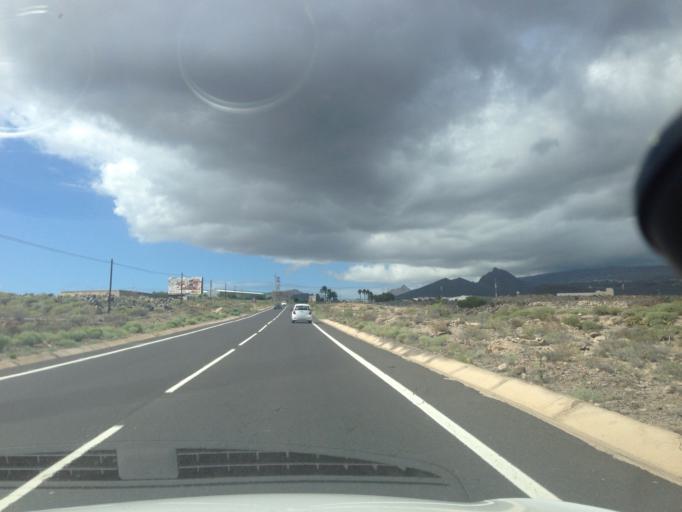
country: ES
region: Canary Islands
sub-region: Provincia de Santa Cruz de Tenerife
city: San Miguel
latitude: 28.0445
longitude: -16.6074
